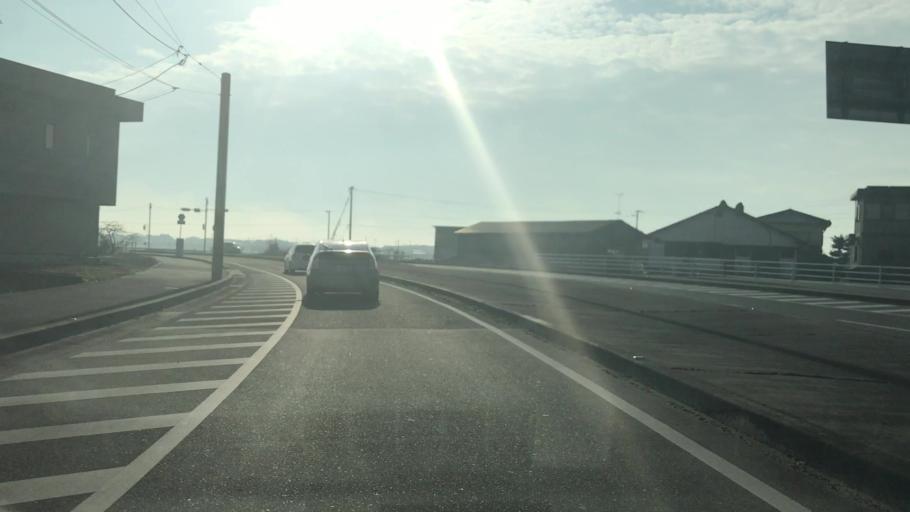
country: JP
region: Saga Prefecture
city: Saga-shi
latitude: 33.2181
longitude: 130.1702
